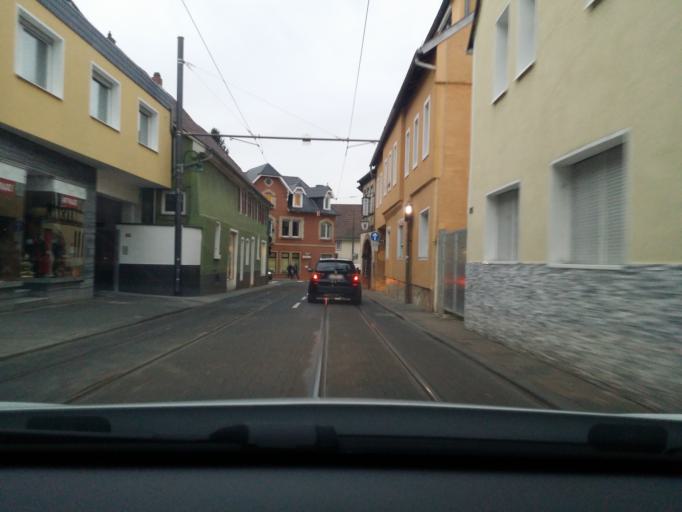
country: DE
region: Hesse
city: Pfungstadt
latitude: 49.8182
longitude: 8.6442
